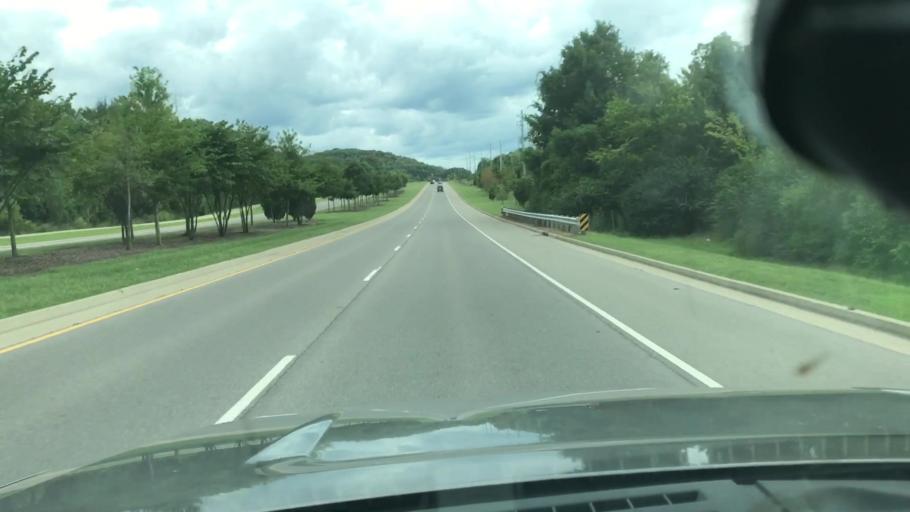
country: US
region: Tennessee
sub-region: Williamson County
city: Franklin
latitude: 35.9218
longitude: -86.8435
